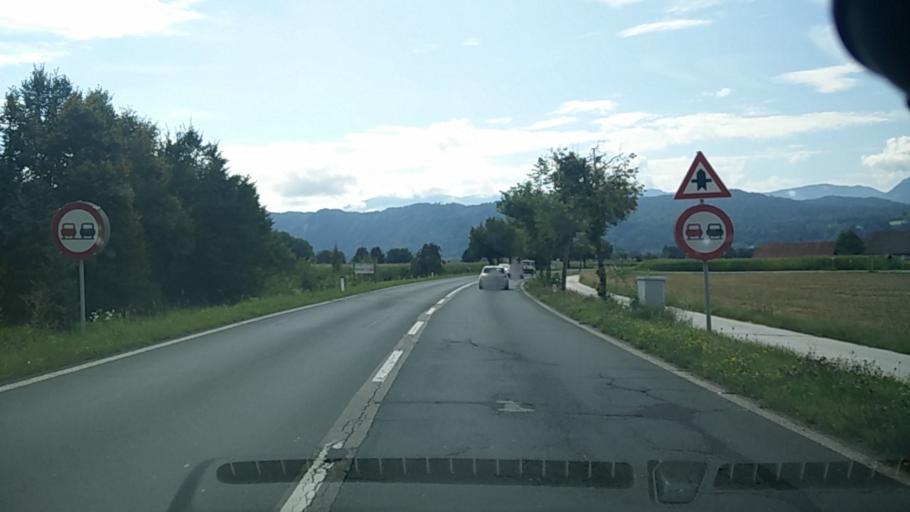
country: AT
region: Carinthia
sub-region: Politischer Bezirk Klagenfurt Land
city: Ebenthal
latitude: 46.6229
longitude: 14.3484
